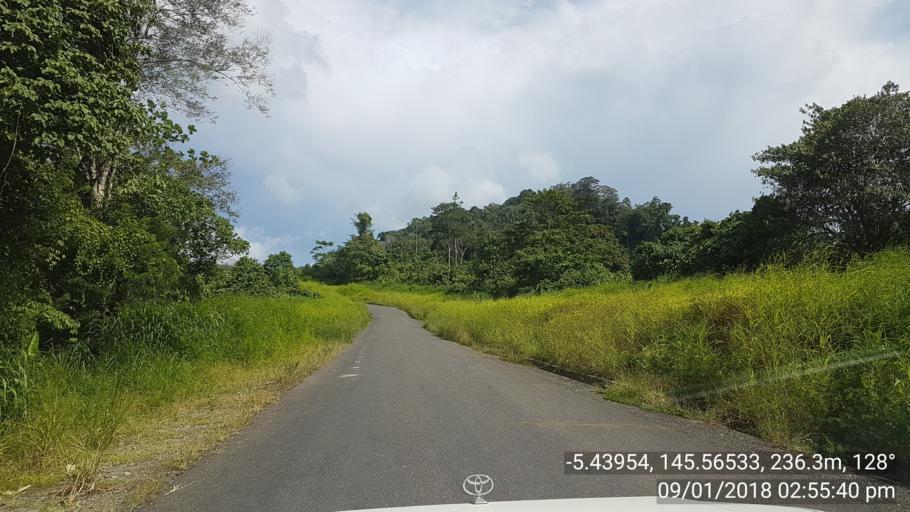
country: PG
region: Madang
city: Madang
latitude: -5.4395
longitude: 145.5652
